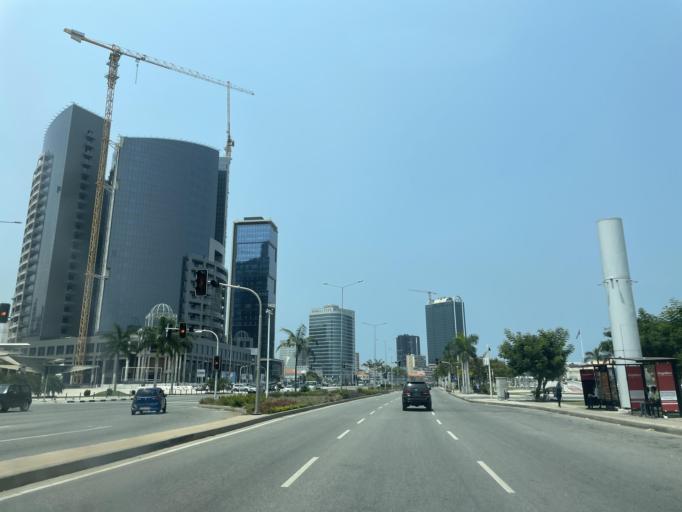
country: AO
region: Luanda
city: Luanda
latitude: -8.8099
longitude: 13.2342
